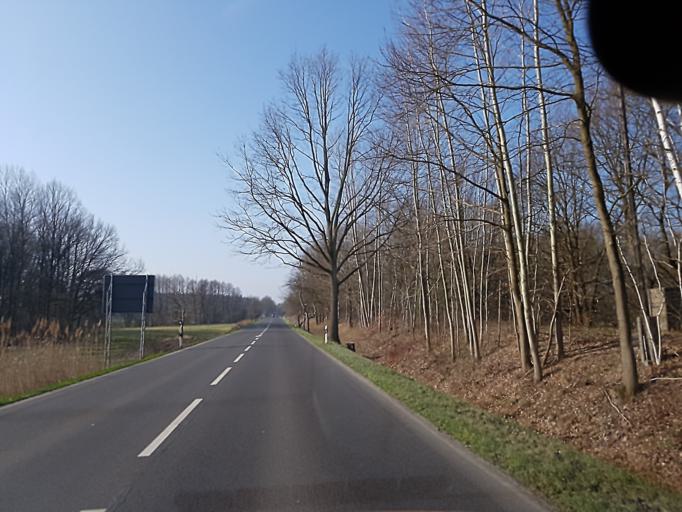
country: DE
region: Brandenburg
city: Forst
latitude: 51.6892
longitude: 14.6018
